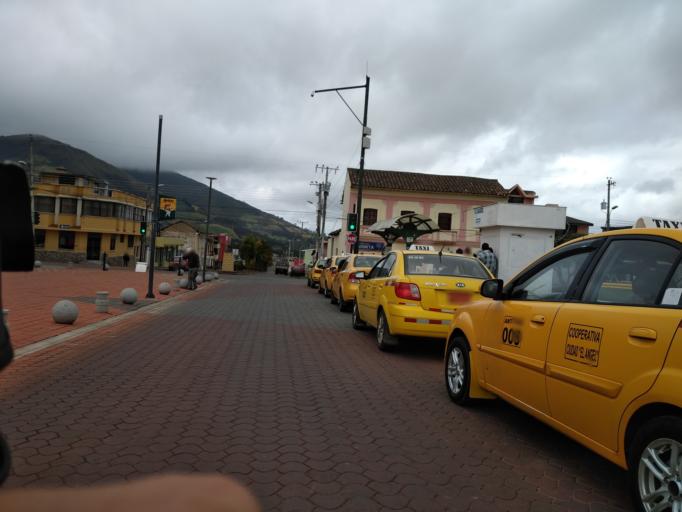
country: EC
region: Carchi
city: El Angel
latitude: 0.6217
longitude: -77.9418
